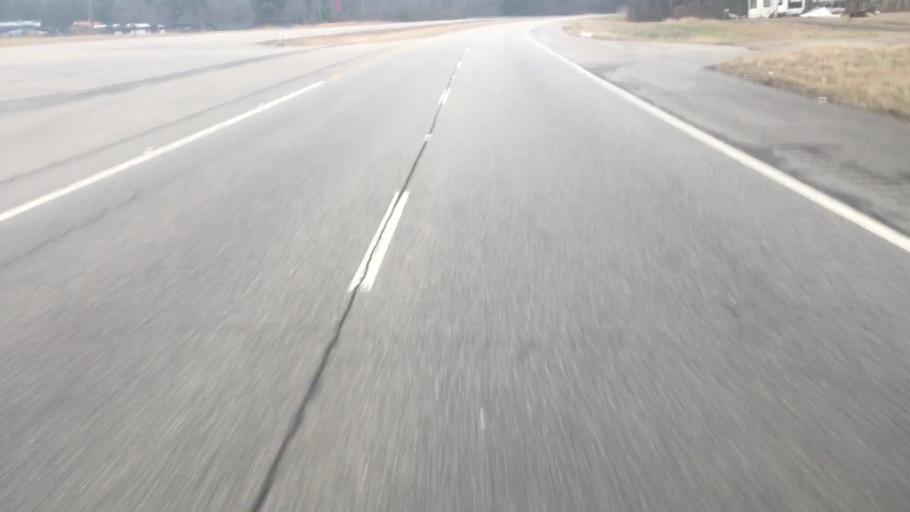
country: US
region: Alabama
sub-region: Walker County
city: Sumiton
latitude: 33.7743
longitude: -87.0757
